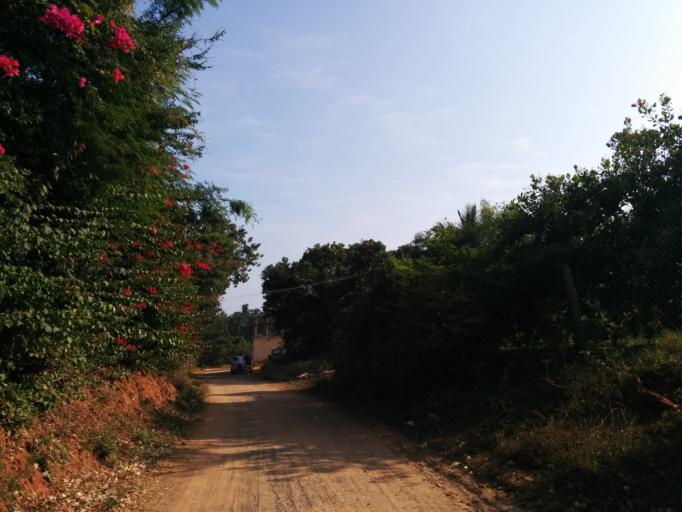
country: IN
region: Tamil Nadu
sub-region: Villupuram
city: Auroville
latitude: 11.9841
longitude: 79.8336
